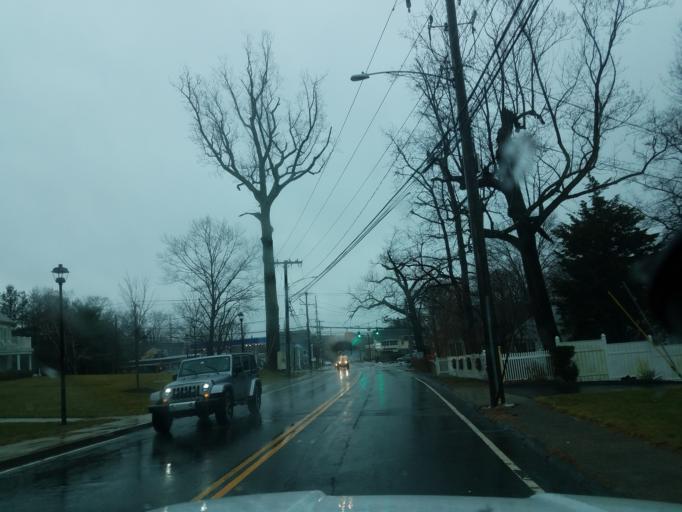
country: US
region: Connecticut
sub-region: Fairfield County
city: Darien
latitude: 41.0713
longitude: -73.4913
